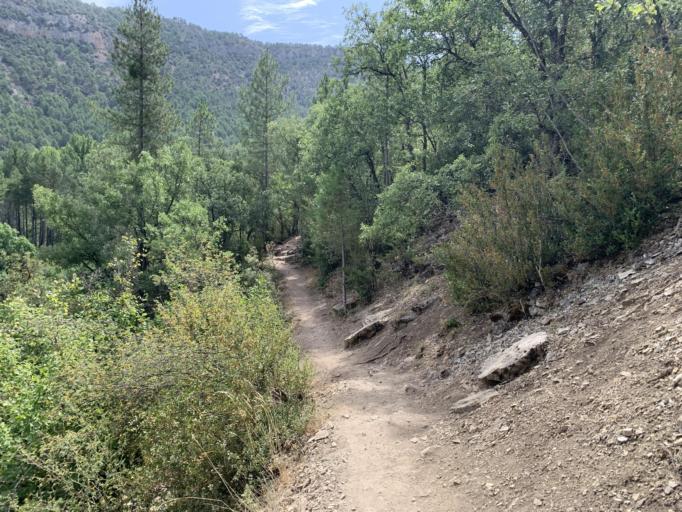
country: ES
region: Castille-La Mancha
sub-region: Provincia de Guadalajara
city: Taravilla
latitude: 40.6475
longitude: -1.9778
